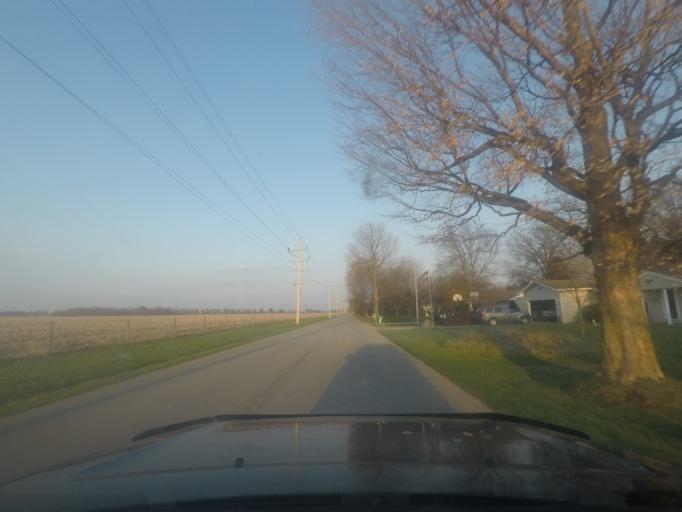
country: US
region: Indiana
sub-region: LaPorte County
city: LaPorte
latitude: 41.5692
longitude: -86.7117
